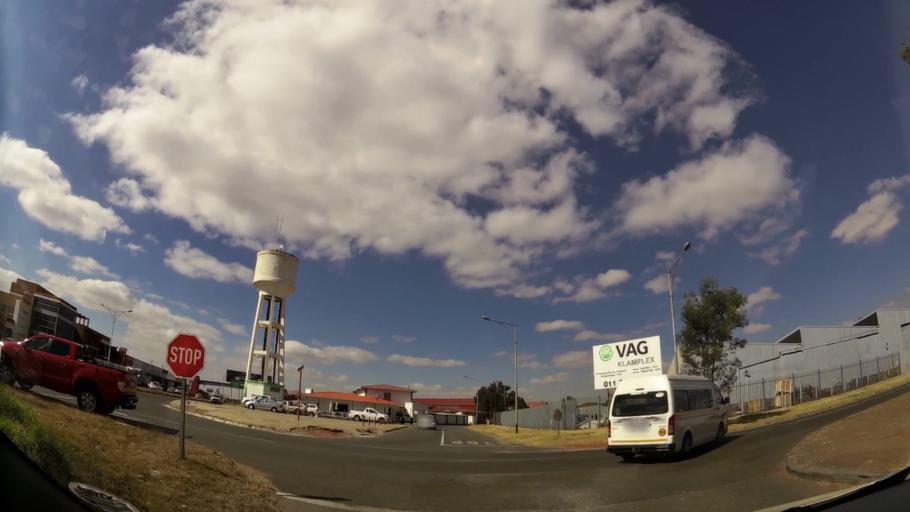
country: ZA
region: Gauteng
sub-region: West Rand District Municipality
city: Krugersdorp
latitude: -26.1132
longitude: 27.8100
